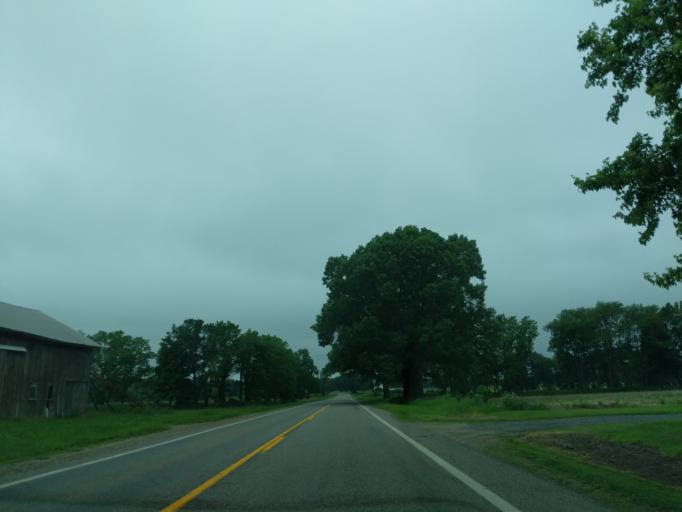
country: US
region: Michigan
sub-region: Hillsdale County
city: Litchfield
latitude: 42.0830
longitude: -84.8028
